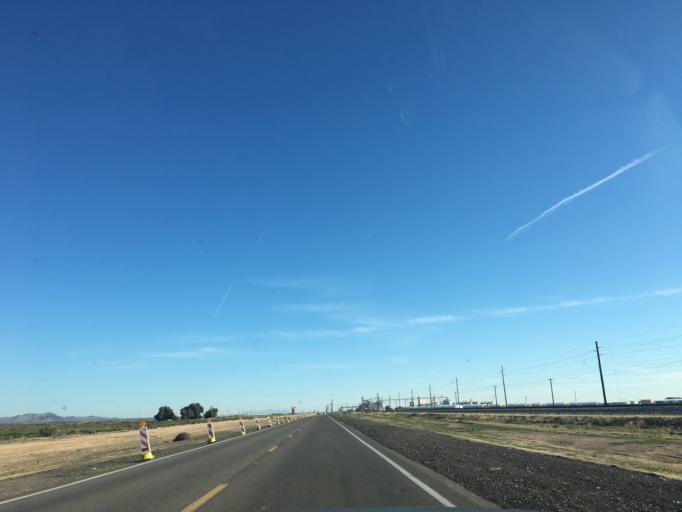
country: US
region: Arizona
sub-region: Pinal County
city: Maricopa
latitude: 33.0235
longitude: -111.9941
